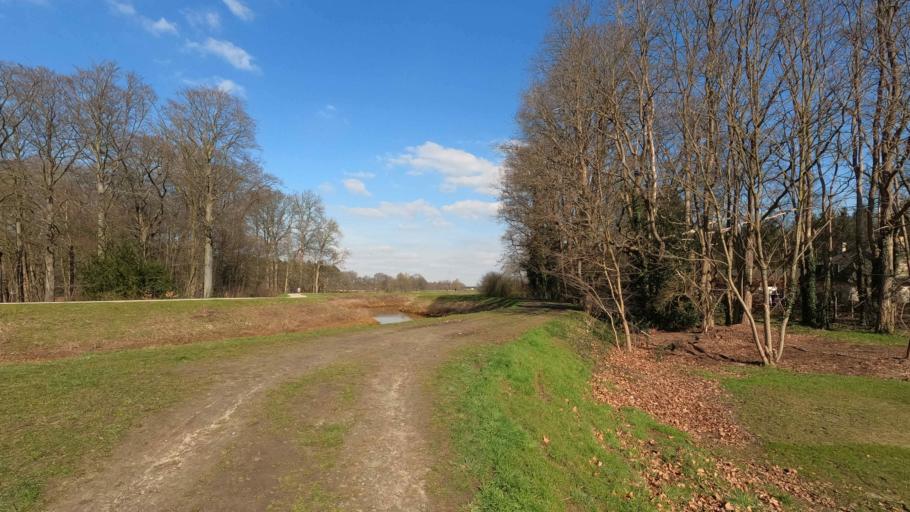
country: BE
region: Flanders
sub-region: Provincie Antwerpen
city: Berlaar
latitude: 51.1273
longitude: 4.6515
